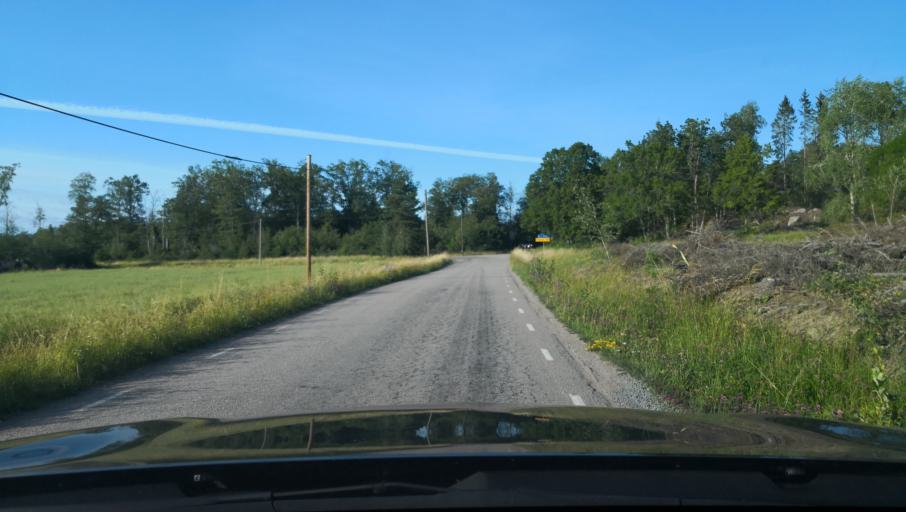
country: SE
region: Uppsala
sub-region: Uppsala Kommun
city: Vattholma
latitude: 59.9163
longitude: 17.8420
